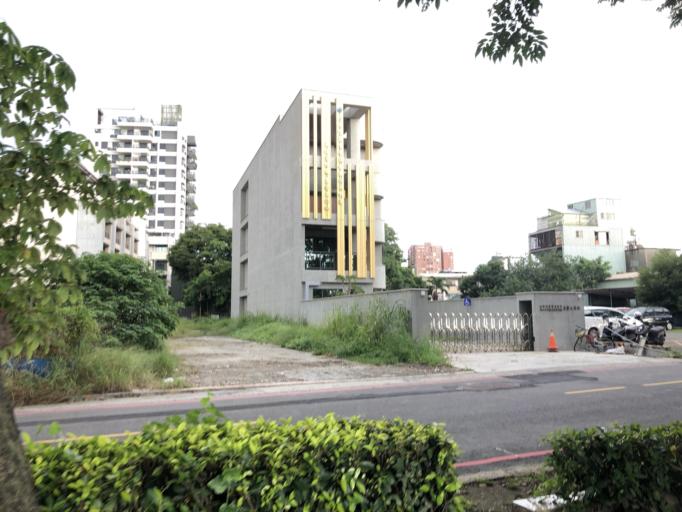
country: TW
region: Kaohsiung
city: Kaohsiung
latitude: 22.6865
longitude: 120.3000
